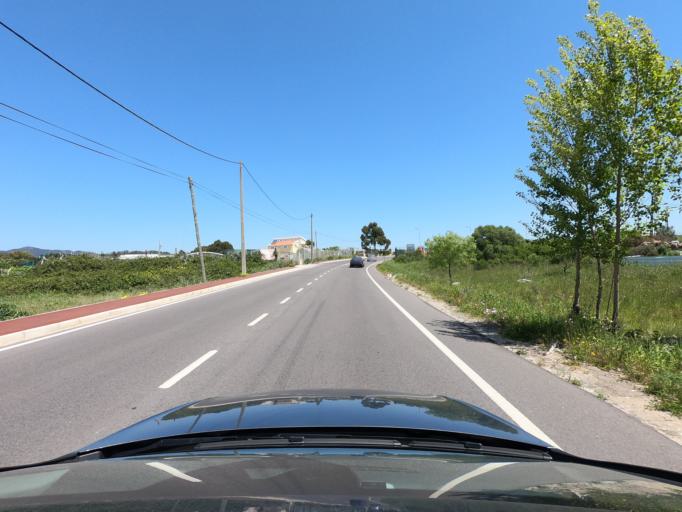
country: PT
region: Lisbon
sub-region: Cascais
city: Parede
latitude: 38.7314
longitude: -9.3598
